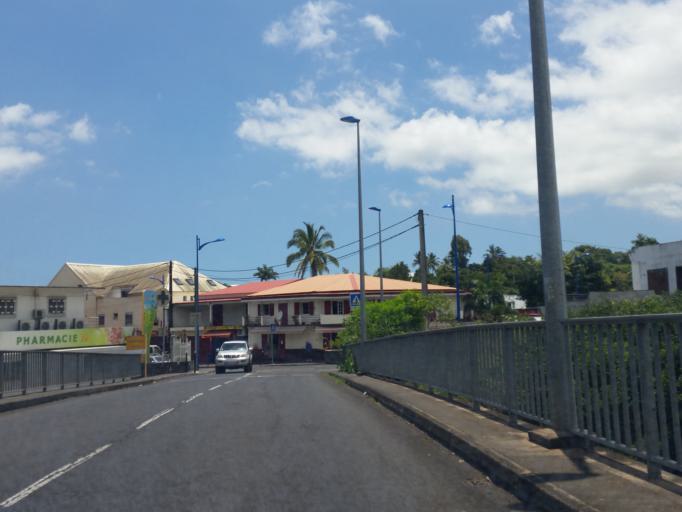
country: RE
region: Reunion
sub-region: Reunion
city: Sainte-Marie
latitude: -20.9165
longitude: 55.5096
